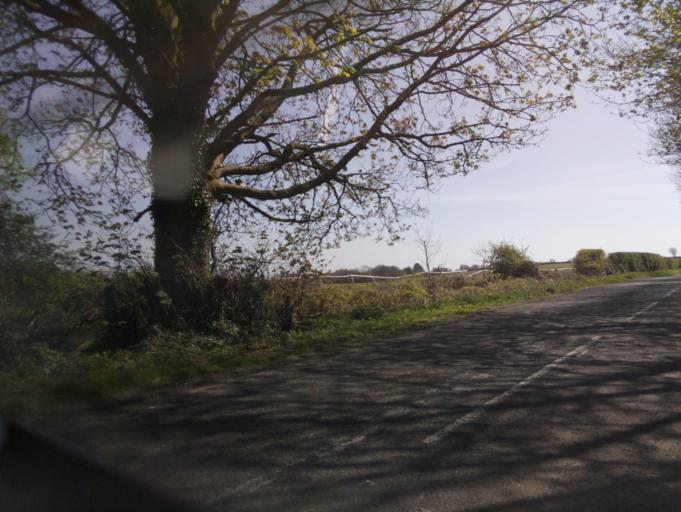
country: GB
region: Wales
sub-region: Newport
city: Llanvaches
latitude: 51.6574
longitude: -2.7917
